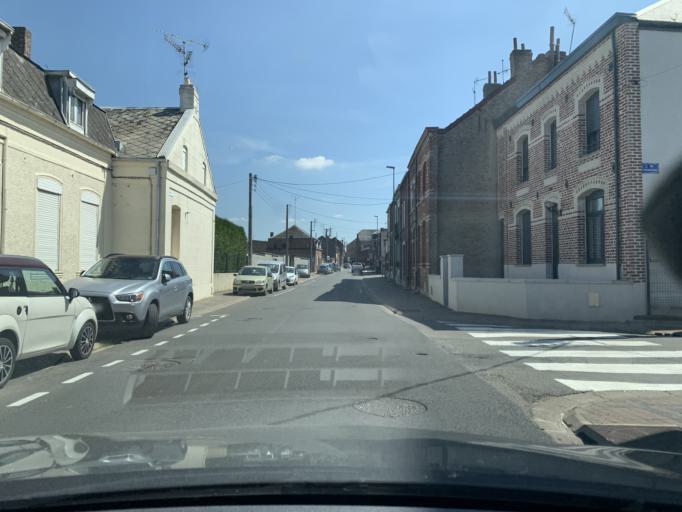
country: FR
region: Nord-Pas-de-Calais
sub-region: Departement du Nord
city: Caudry
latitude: 50.1223
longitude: 3.4017
